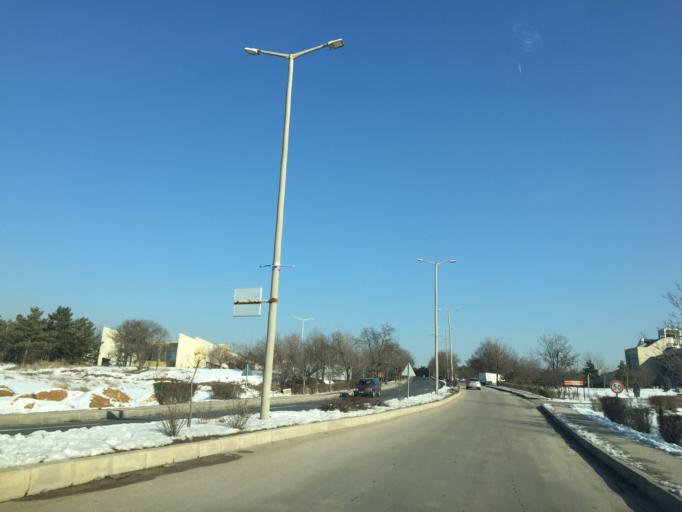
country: TR
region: Ankara
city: Ankara
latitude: 39.8997
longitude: 32.7771
